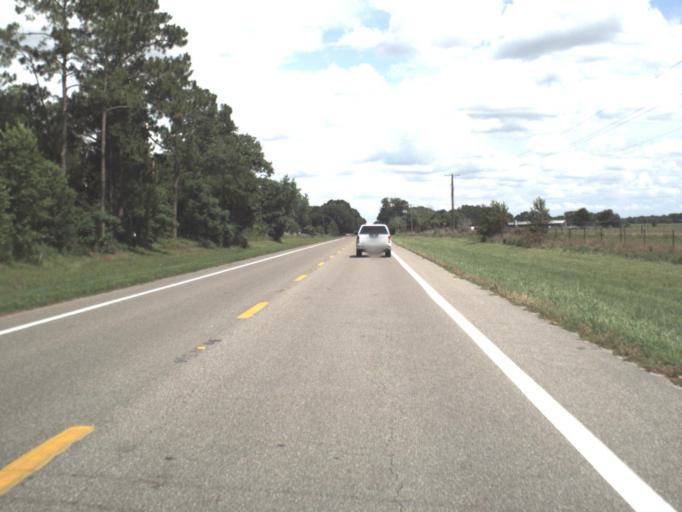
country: US
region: Florida
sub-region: Lafayette County
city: Mayo
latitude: 29.9889
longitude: -83.0054
